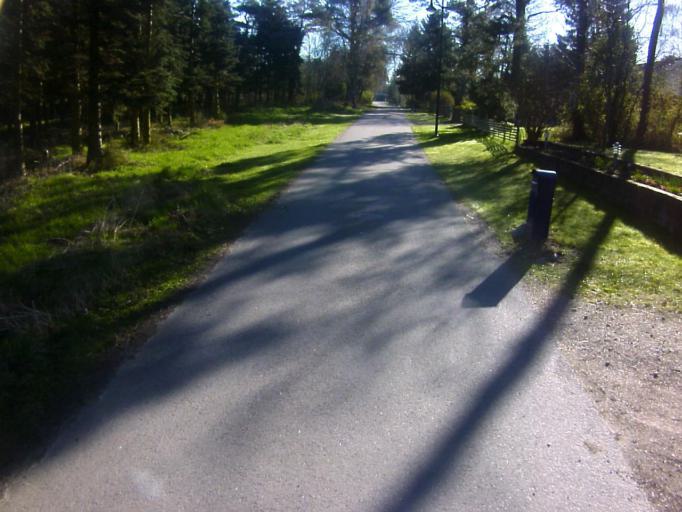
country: SE
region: Skane
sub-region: Kavlinge Kommun
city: Hofterup
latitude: 55.8176
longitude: 12.9698
